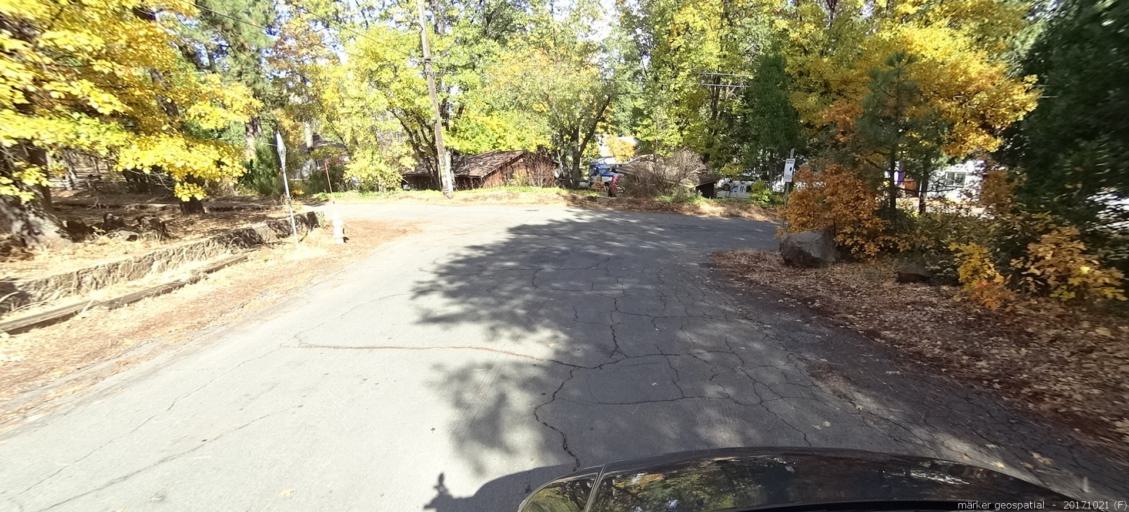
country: US
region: California
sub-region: Shasta County
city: Burney
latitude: 40.8819
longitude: -121.6747
